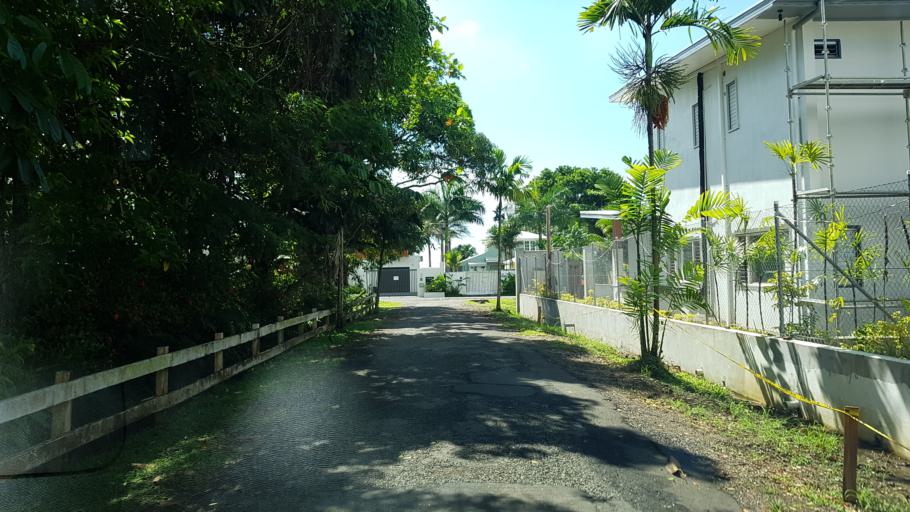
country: FJ
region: Central
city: Suva
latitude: -18.1466
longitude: 178.4551
